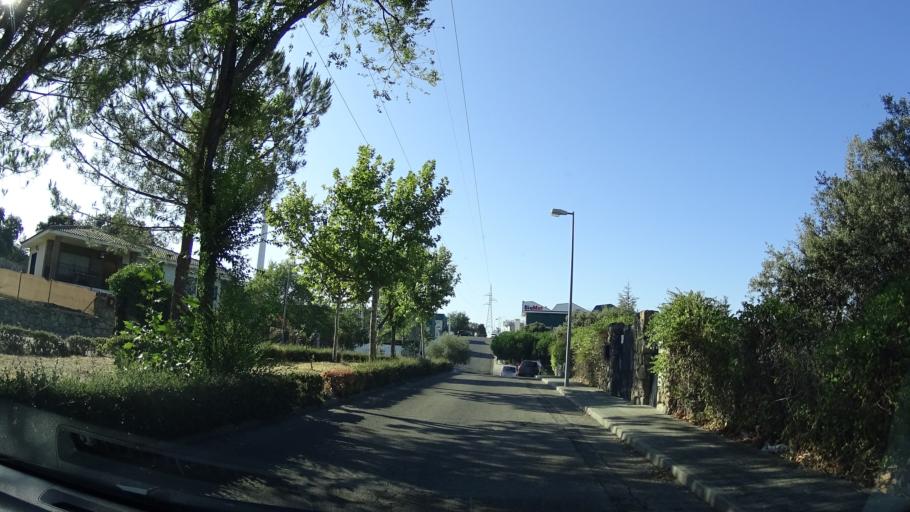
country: ES
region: Madrid
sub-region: Provincia de Madrid
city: Colmenarejo
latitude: 40.5547
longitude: -4.0217
